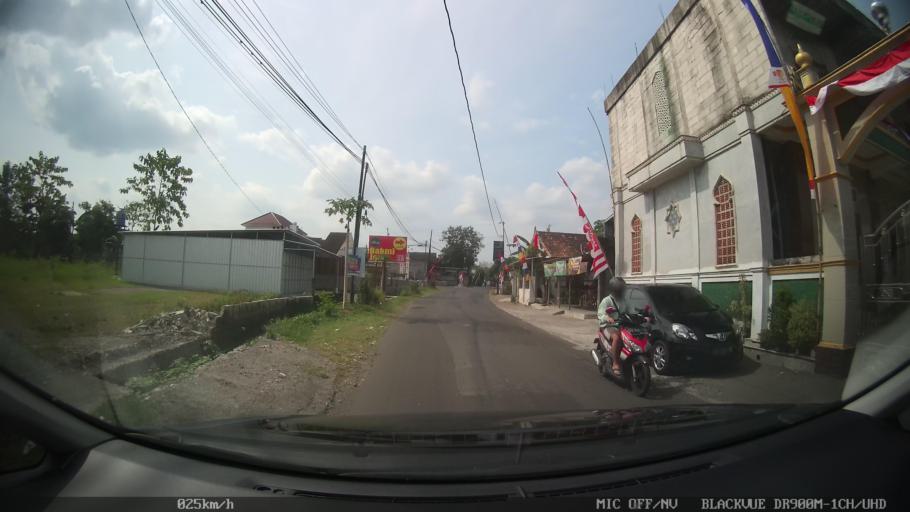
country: ID
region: Daerah Istimewa Yogyakarta
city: Depok
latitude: -7.7922
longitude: 110.4461
